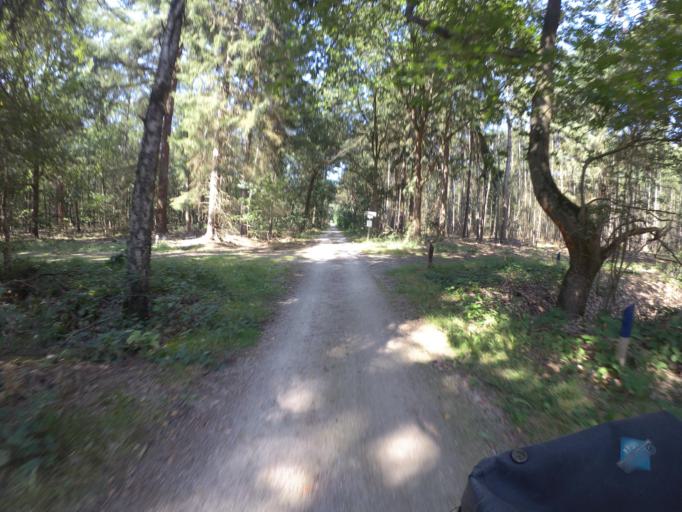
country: NL
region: North Brabant
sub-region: Gemeente Mill en Sint Hubert
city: Wilbertoord
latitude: 51.6147
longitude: 5.8012
